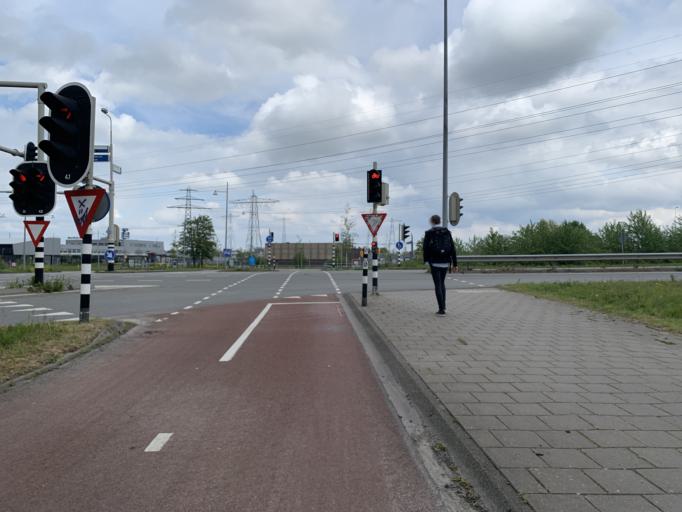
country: NL
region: Groningen
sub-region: Gemeente Groningen
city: Oosterpark
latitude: 53.2085
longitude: 6.5927
